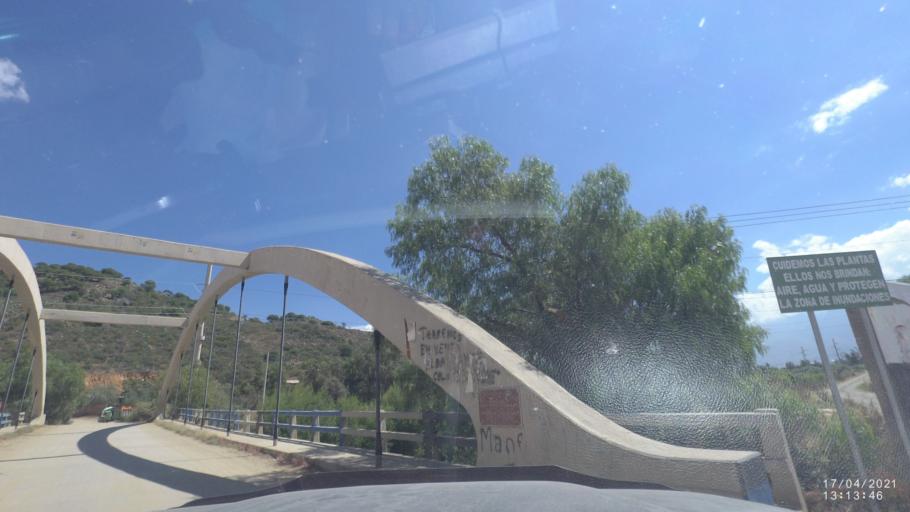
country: BO
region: Cochabamba
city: Cochabamba
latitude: -17.4177
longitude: -66.2243
